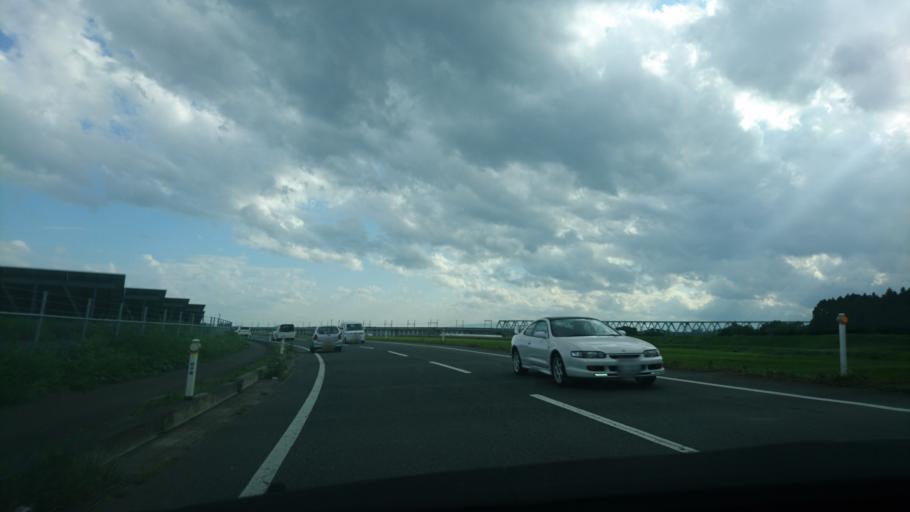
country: JP
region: Iwate
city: Kitakami
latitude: 39.2485
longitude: 141.1181
